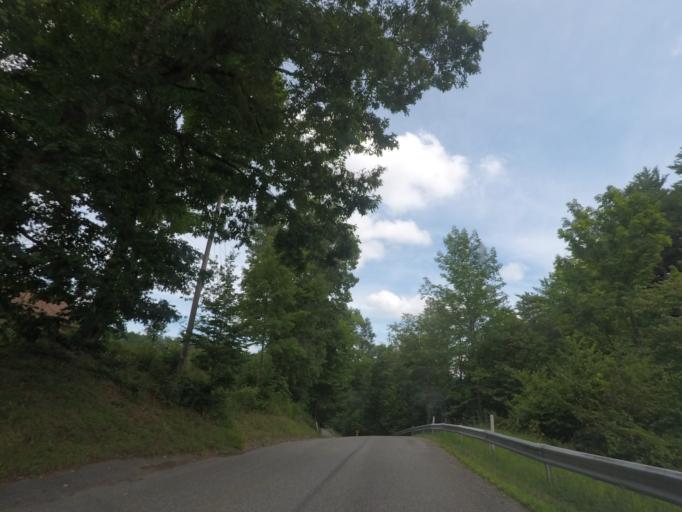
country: US
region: New York
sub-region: Saratoga County
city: Stillwater
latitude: 43.0090
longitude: -73.6233
